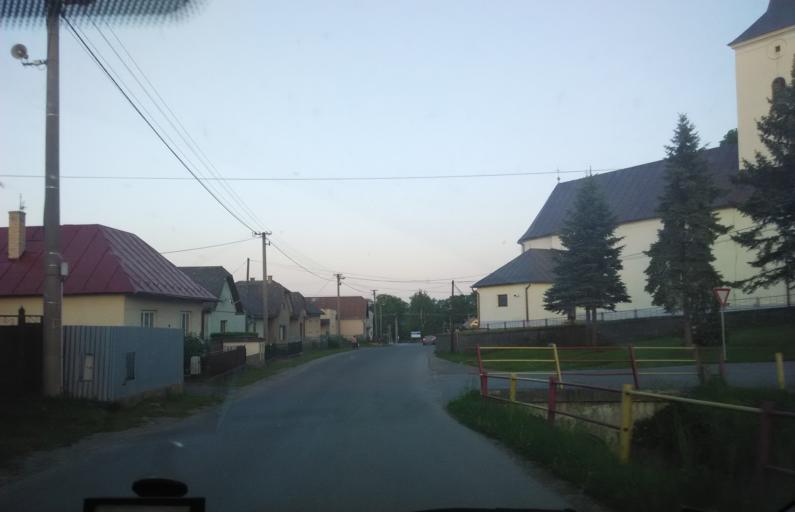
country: SK
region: Presovsky
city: Sabinov
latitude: 49.0570
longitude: 21.0591
